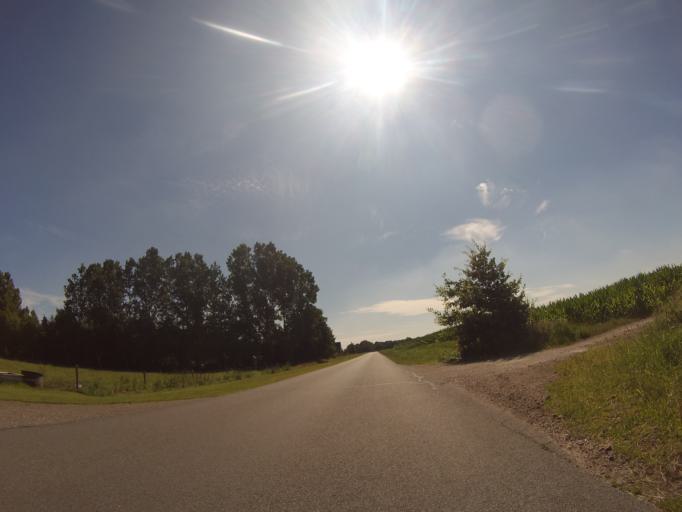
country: NL
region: Drenthe
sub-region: Gemeente Emmen
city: Klazienaveen
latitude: 52.6931
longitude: 6.9427
